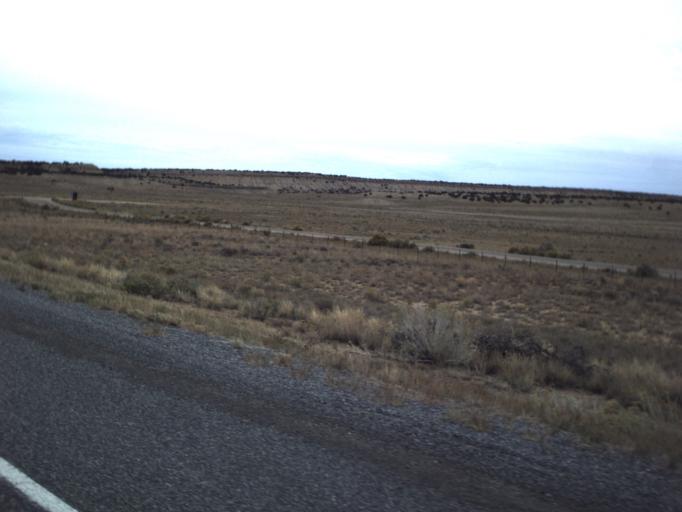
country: US
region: Utah
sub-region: Emery County
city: Castle Dale
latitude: 38.8783
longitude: -110.6624
